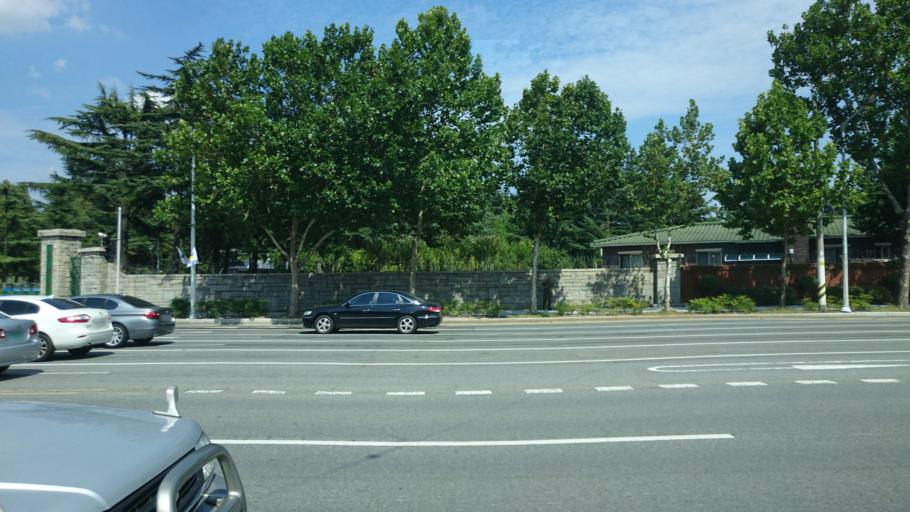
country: KR
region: Daegu
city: Daegu
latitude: 35.8700
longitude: 128.6487
